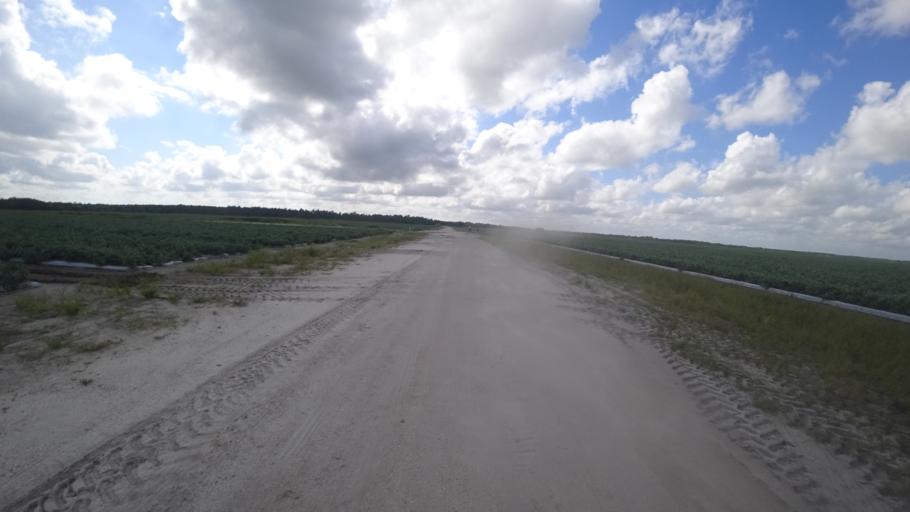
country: US
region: Florida
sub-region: Sarasota County
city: Lake Sarasota
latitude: 27.4113
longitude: -82.1999
